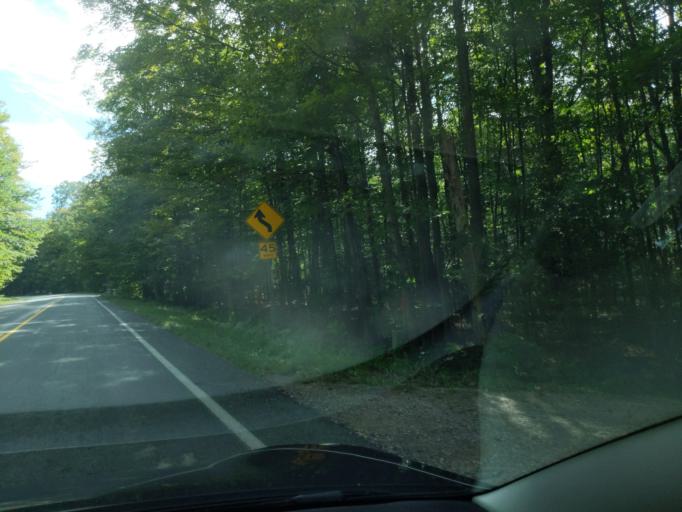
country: US
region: Michigan
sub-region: Antrim County
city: Bellaire
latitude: 45.0277
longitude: -85.2958
